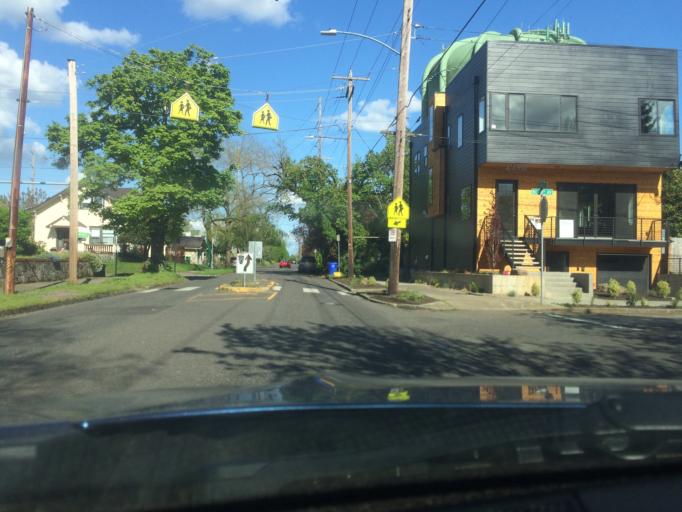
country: US
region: Oregon
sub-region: Multnomah County
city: Portland
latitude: 45.5554
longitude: -122.6474
